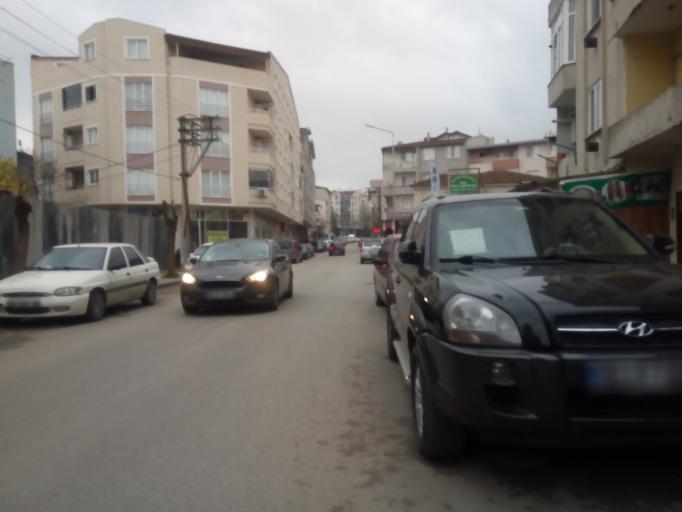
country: TR
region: Bursa
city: Niluefer
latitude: 40.2551
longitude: 28.9617
